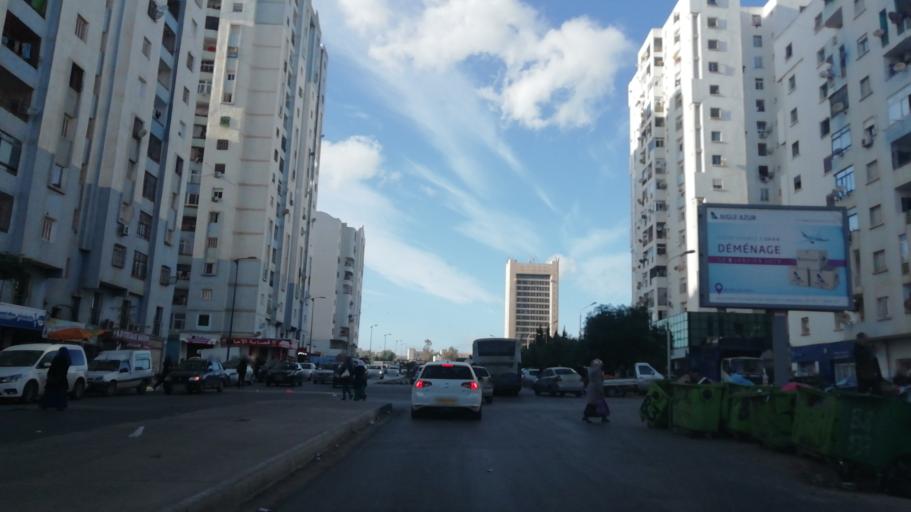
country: DZ
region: Oran
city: Bir el Djir
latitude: 35.7013
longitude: -0.5755
